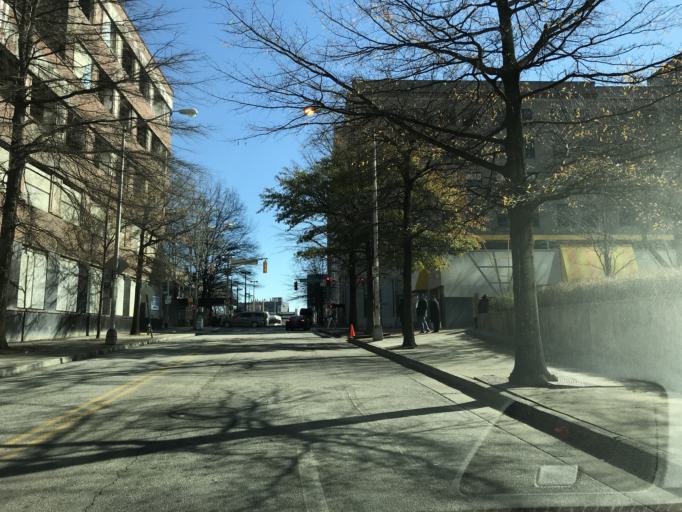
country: US
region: Georgia
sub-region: Fulton County
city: Atlanta
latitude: 33.7542
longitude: -84.3932
